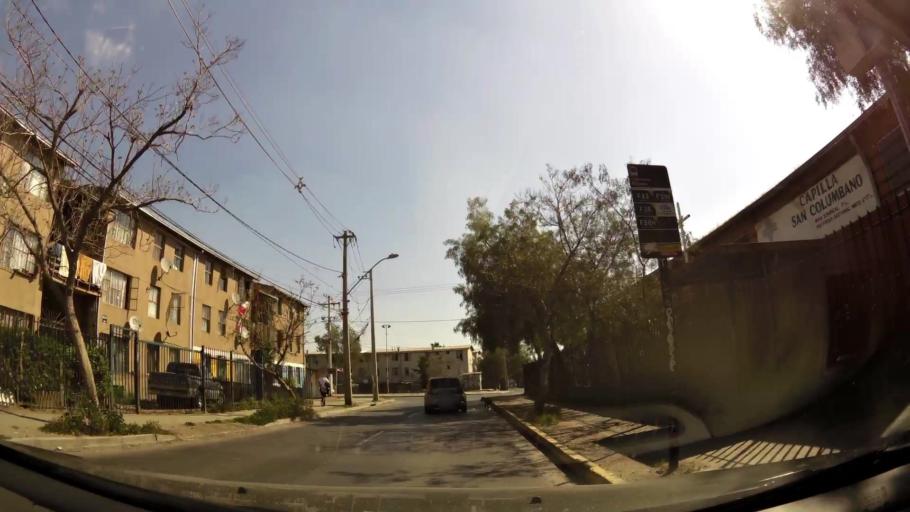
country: CL
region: Santiago Metropolitan
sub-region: Provincia de Santiago
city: La Pintana
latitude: -33.6262
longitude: -70.6192
